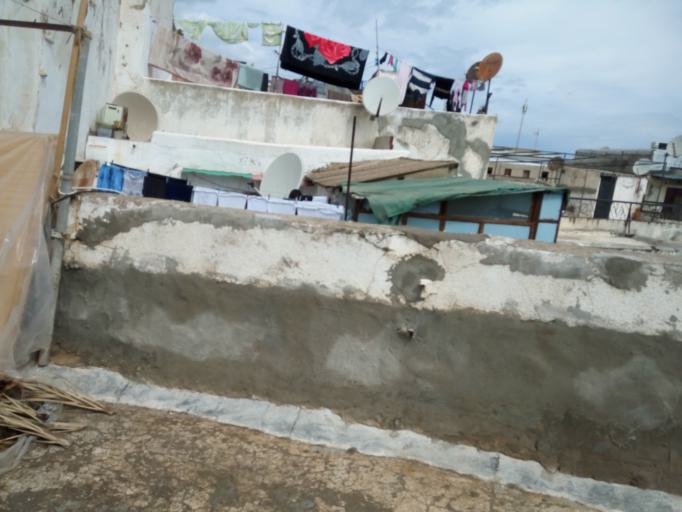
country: DZ
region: Alger
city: Algiers
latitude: 36.7856
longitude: 3.0575
